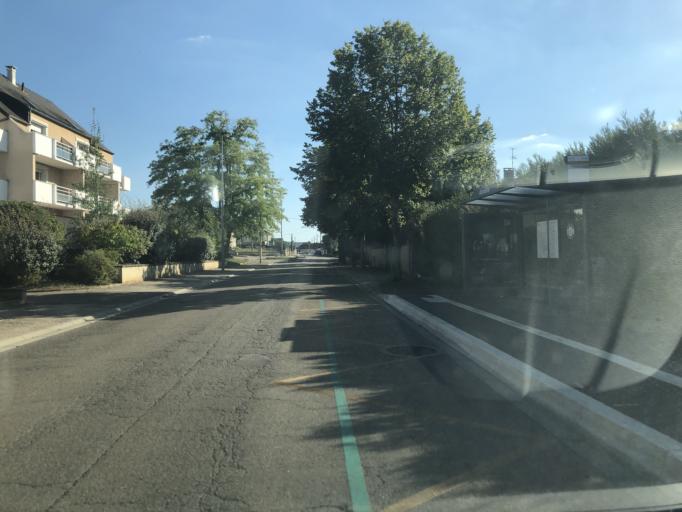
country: FR
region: Bourgogne
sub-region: Departement de l'Yonne
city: Auxerre
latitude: 47.7992
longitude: 3.5893
